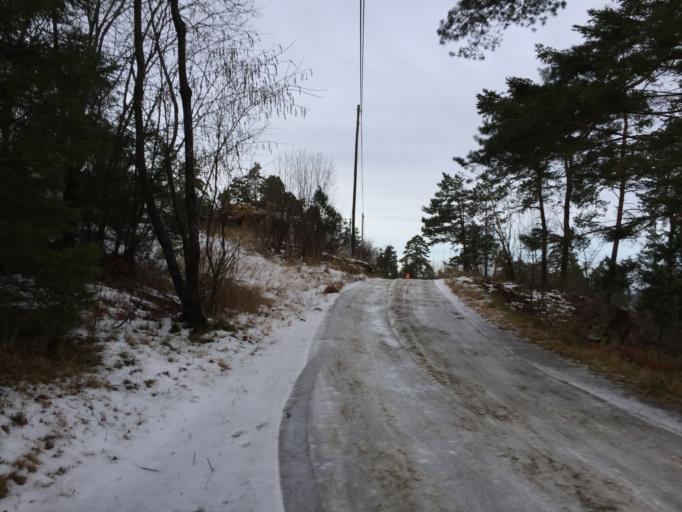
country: NO
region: Ostfold
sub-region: Moss
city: Moss
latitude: 59.4874
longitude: 10.6724
